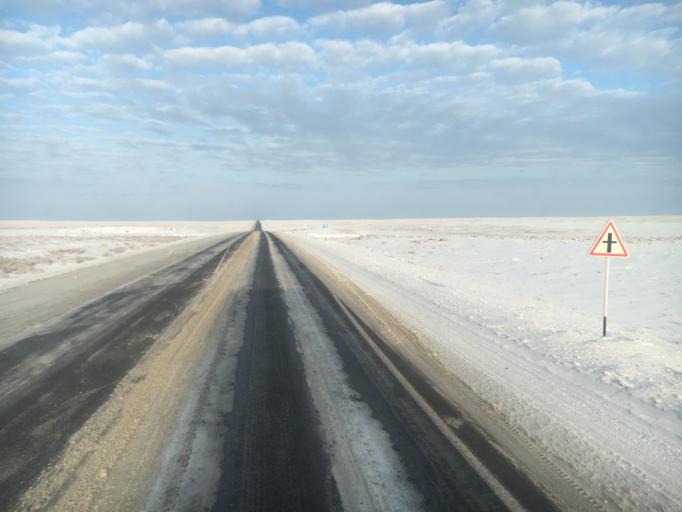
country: KZ
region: Qyzylorda
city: Sekseuil
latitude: 47.6789
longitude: 61.4431
